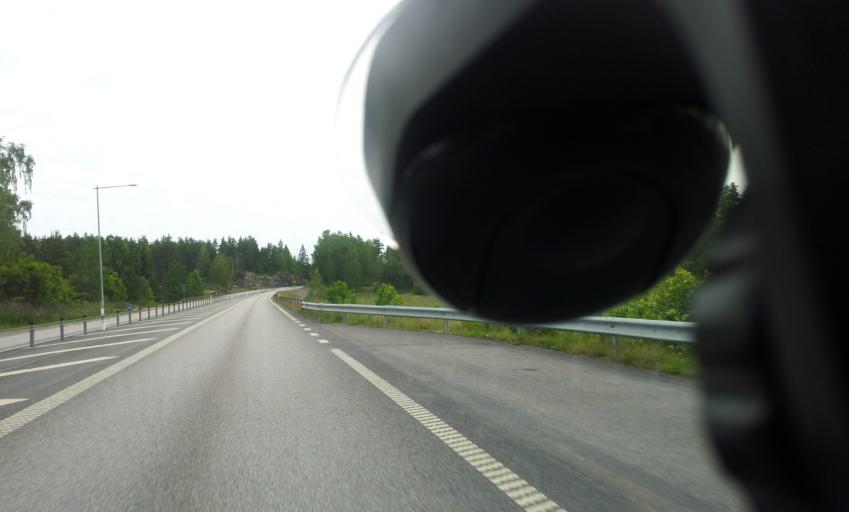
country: SE
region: Kalmar
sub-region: Vasterviks Kommun
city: Forserum
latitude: 57.9798
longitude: 16.4836
